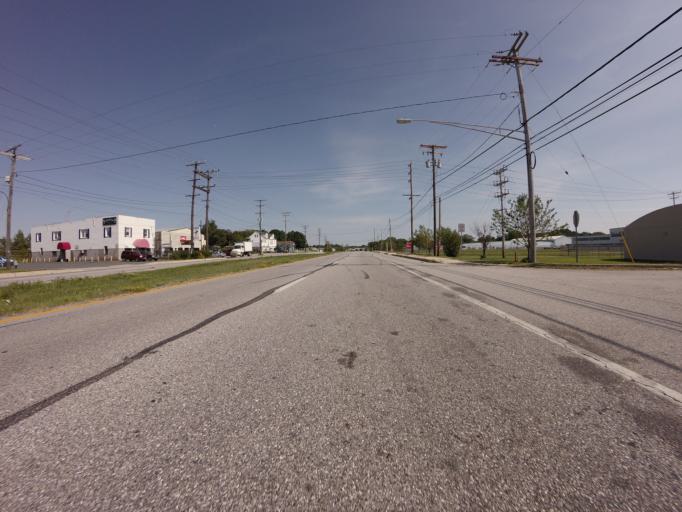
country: US
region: Maryland
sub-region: Baltimore County
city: Edgemere
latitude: 39.2528
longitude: -76.4611
